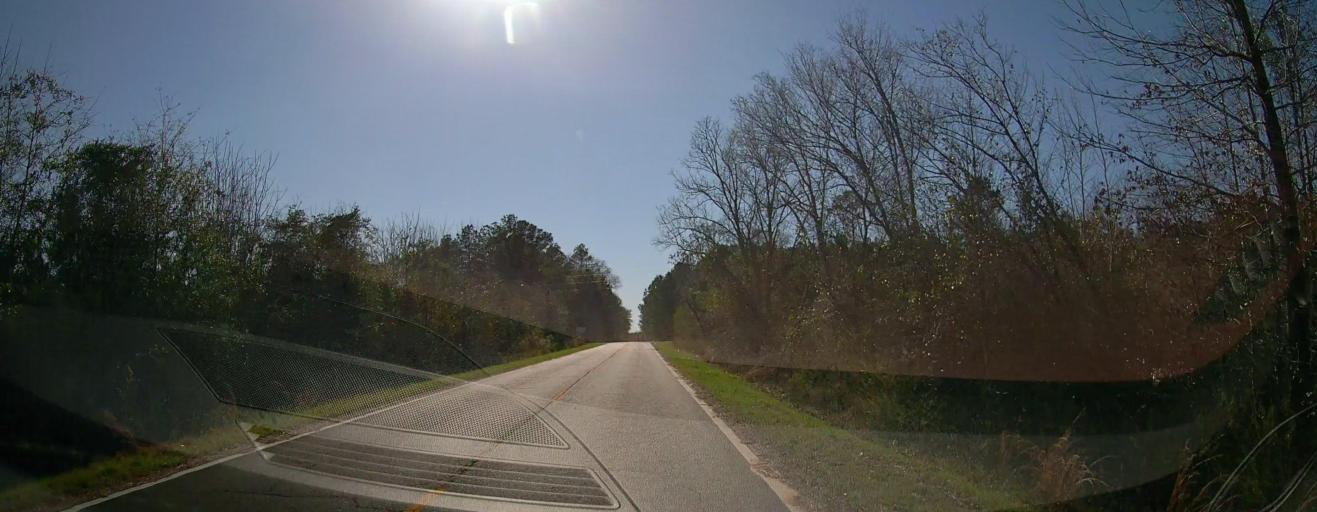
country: US
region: Georgia
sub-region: Taylor County
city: Reynolds
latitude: 32.5474
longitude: -83.9996
